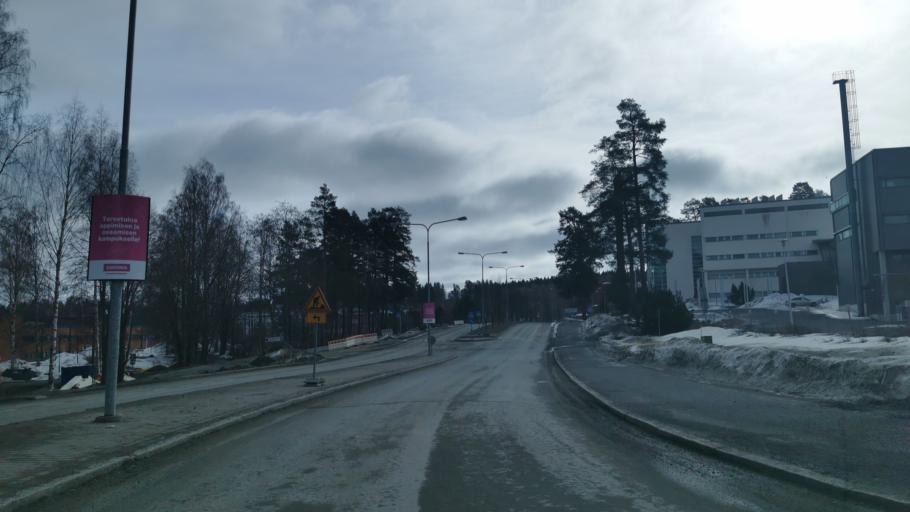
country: FI
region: Northern Savo
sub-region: Kuopio
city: Kuopio
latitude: 62.8911
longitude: 27.6302
